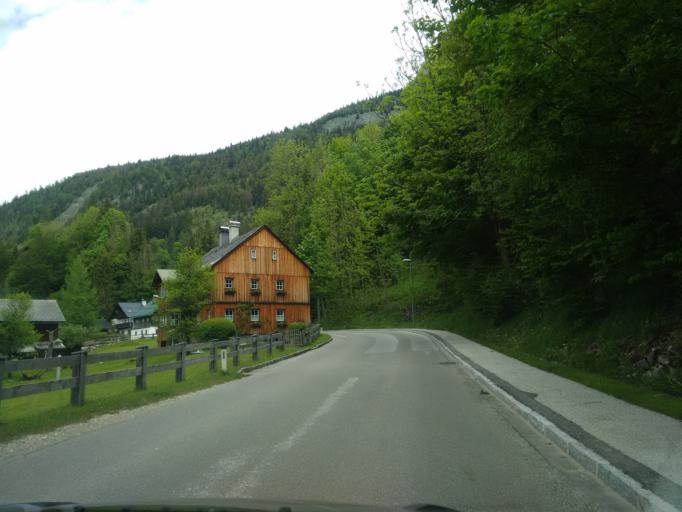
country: AT
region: Styria
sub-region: Politischer Bezirk Liezen
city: Altaussee
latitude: 47.6439
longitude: 13.7620
